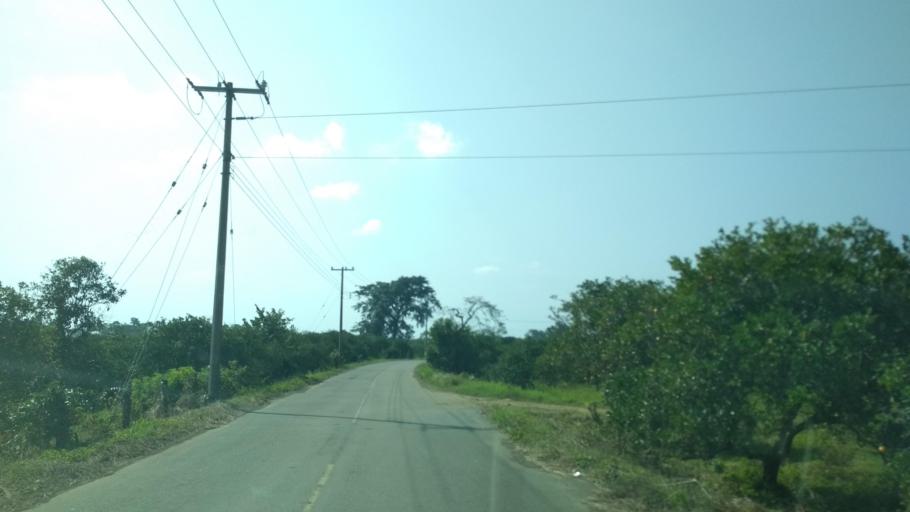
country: MX
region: Puebla
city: San Jose Acateno
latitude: 20.2030
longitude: -97.1793
